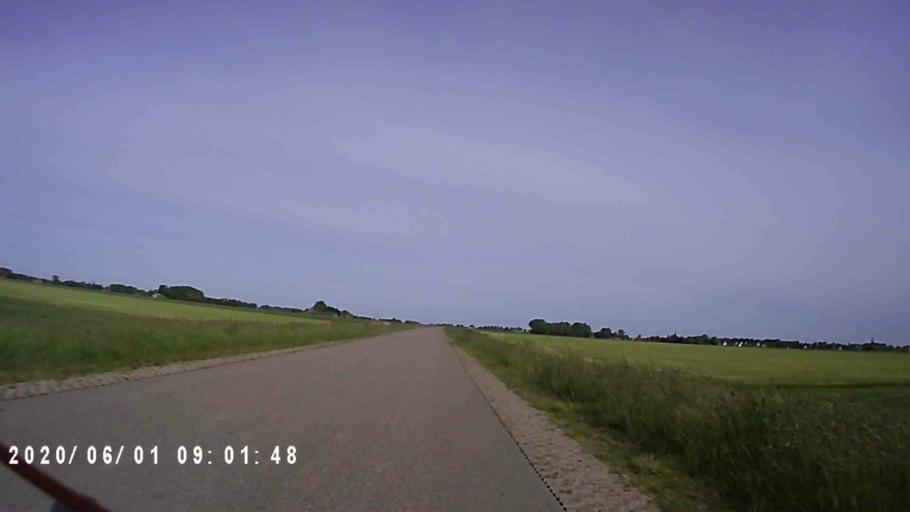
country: NL
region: Friesland
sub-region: Gemeente Ferwerderadiel
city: Hallum
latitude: 53.2919
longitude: 5.7873
